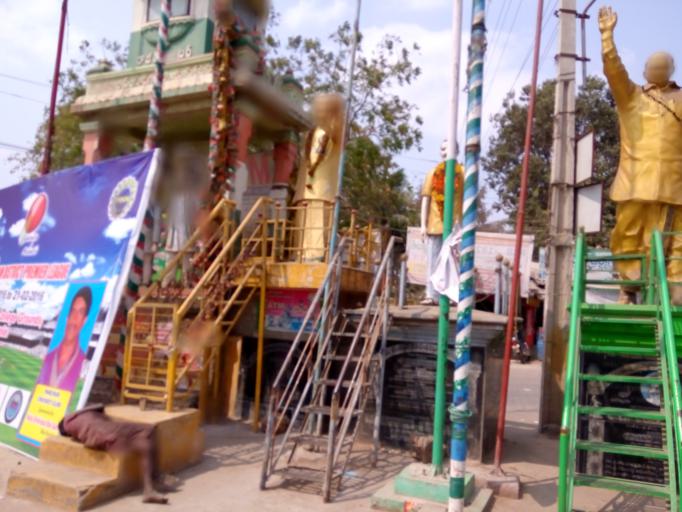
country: IN
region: Andhra Pradesh
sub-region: Prakasam
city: pedda nakkalapalem
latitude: 15.9682
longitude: 80.2768
